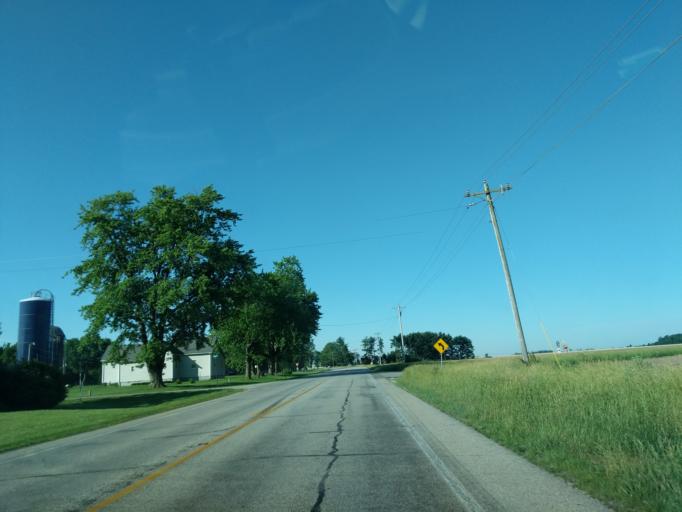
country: US
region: Indiana
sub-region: Shelby County
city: Shelbyville
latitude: 39.5995
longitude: -85.7748
